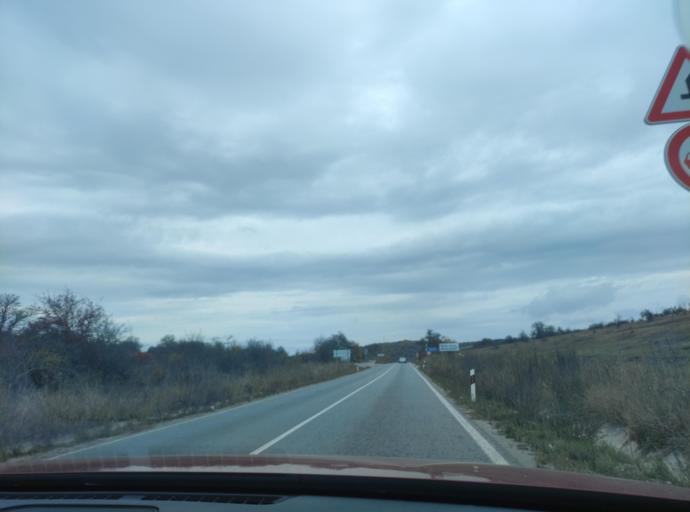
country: BG
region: Sofiya
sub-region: Obshtina Godech
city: Godech
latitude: 42.9591
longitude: 23.1551
